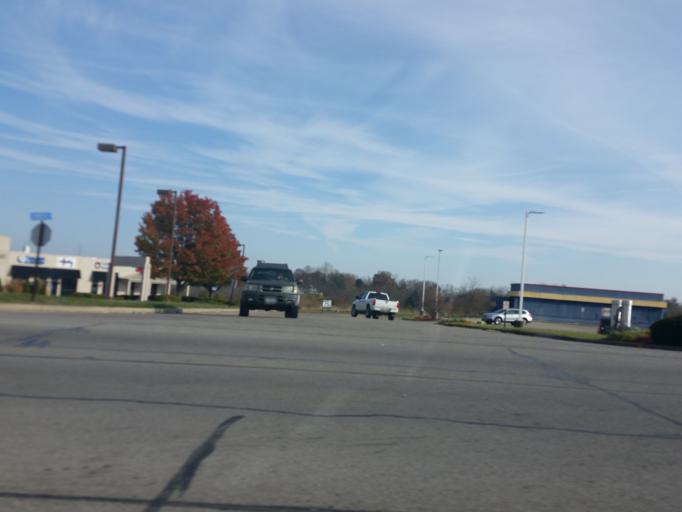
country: US
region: Kentucky
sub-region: Campbell County
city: Alexandria
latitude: 38.9702
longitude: -84.3926
